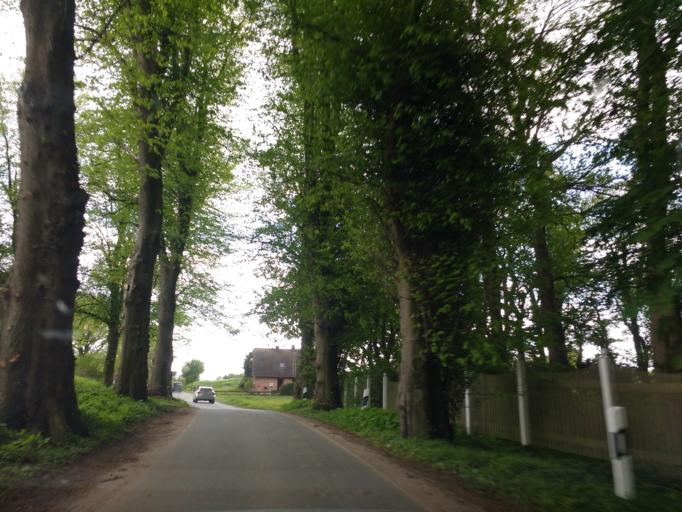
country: DE
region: Schleswig-Holstein
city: Loose
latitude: 54.5003
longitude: 9.8642
